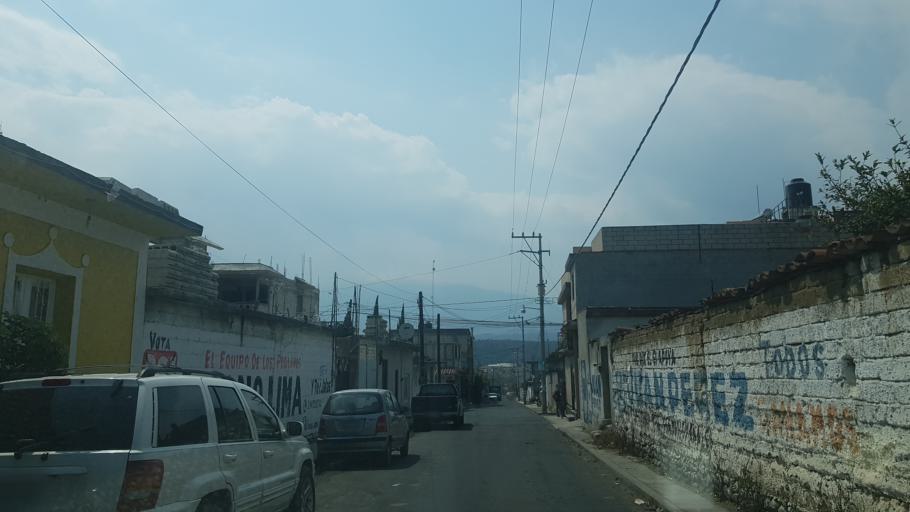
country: MX
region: Puebla
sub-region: Tianguismanalco
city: San Martin Tlapala
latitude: 18.9738
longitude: -98.4499
